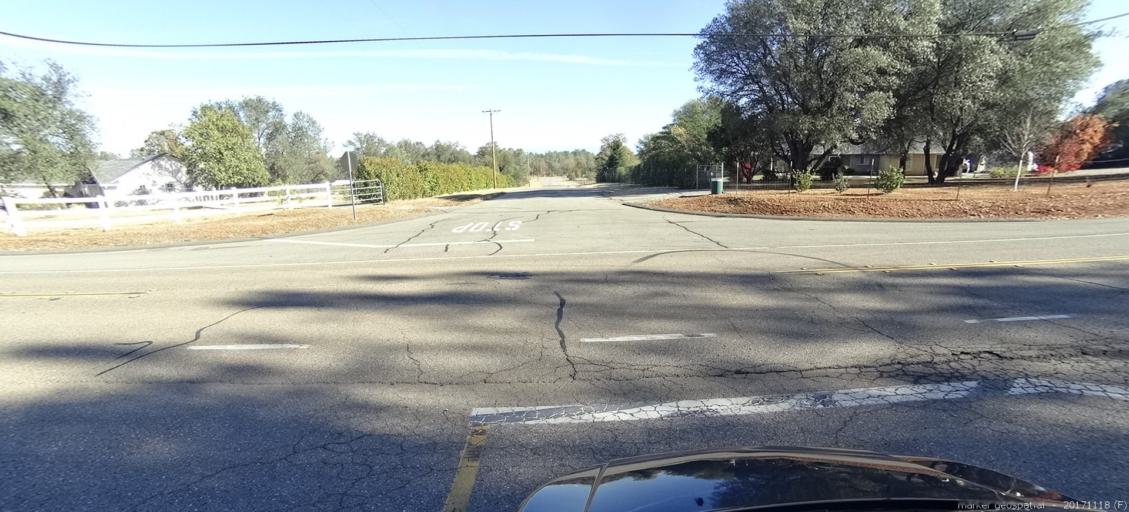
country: US
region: California
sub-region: Shasta County
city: Redding
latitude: 40.4648
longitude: -122.4547
